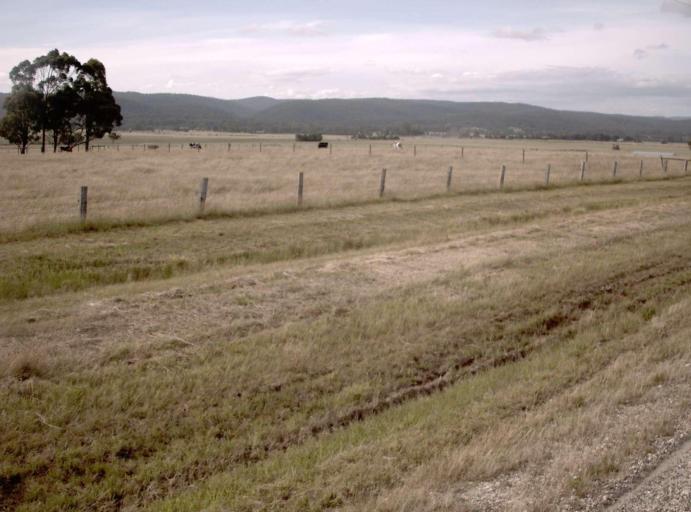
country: AU
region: Victoria
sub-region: Wellington
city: Heyfield
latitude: -38.0258
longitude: 146.6689
